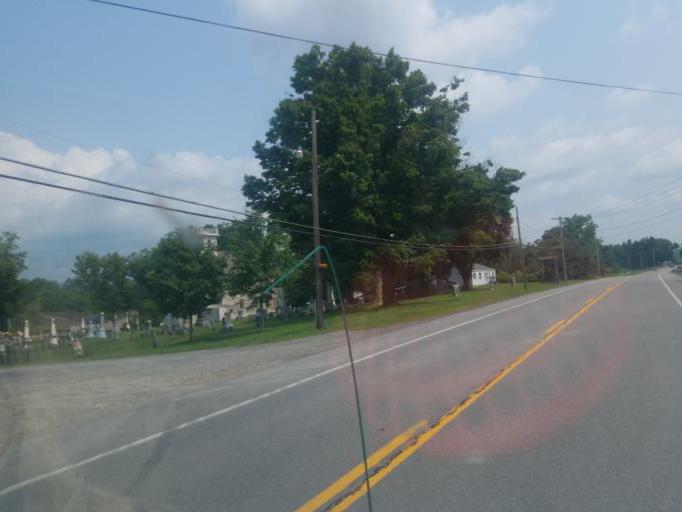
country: US
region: New York
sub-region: Herkimer County
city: Herkimer
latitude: 43.0176
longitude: -74.9551
